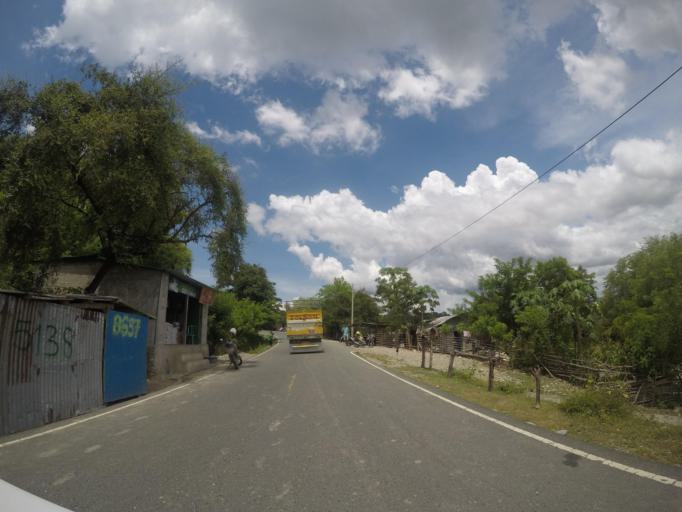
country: TL
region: Bobonaro
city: Maliana
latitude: -8.9530
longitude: 125.1100
